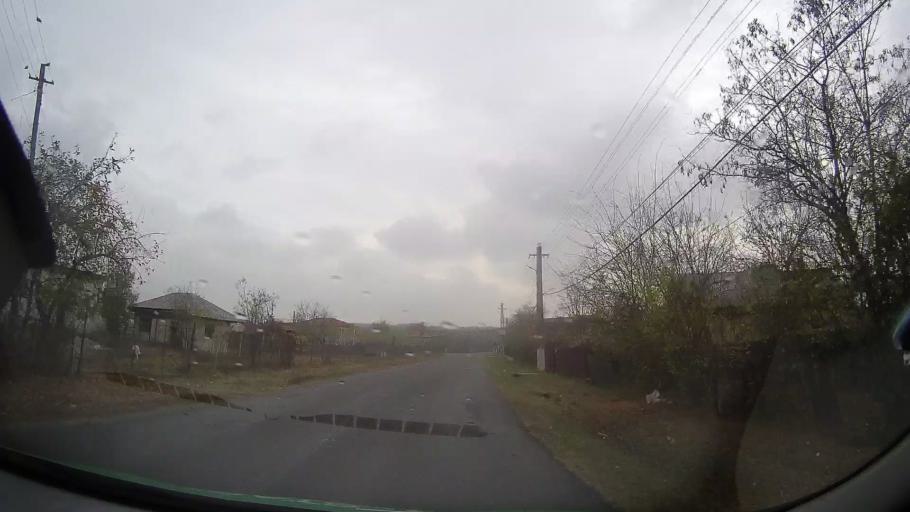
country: RO
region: Prahova
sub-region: Comuna Draganesti
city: Draganesti
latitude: 44.8281
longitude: 26.2815
